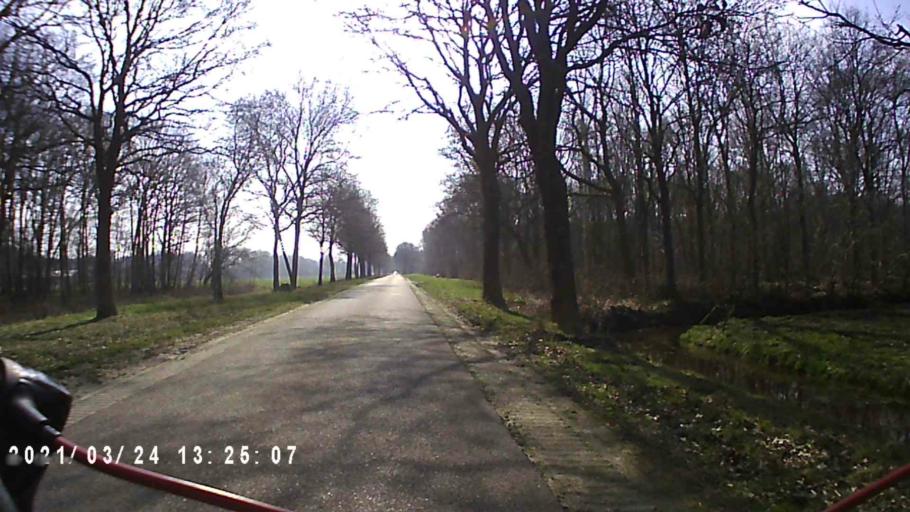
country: NL
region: Groningen
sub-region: Gemeente Grootegast
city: Grootegast
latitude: 53.0945
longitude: 6.2782
